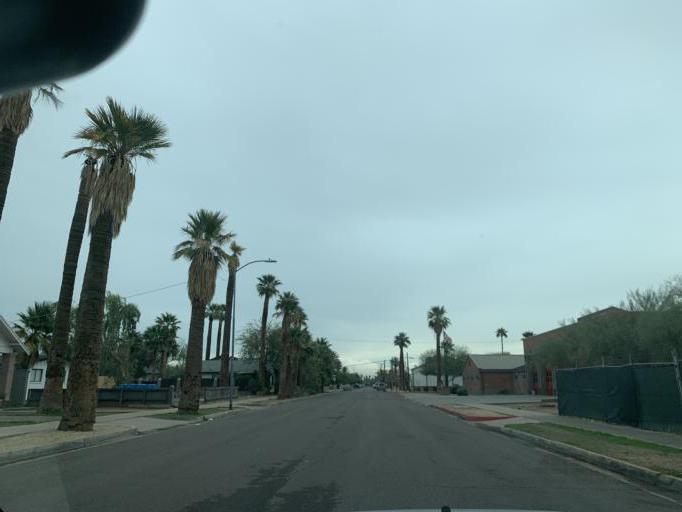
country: US
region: Arizona
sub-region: Maricopa County
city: Phoenix
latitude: 33.4529
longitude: -112.0601
